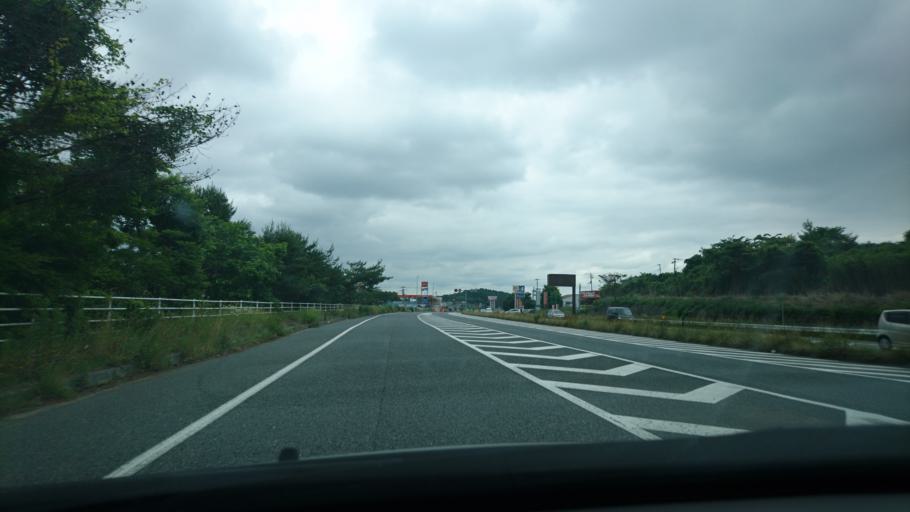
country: JP
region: Miyagi
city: Furukawa
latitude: 38.7085
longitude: 141.0145
